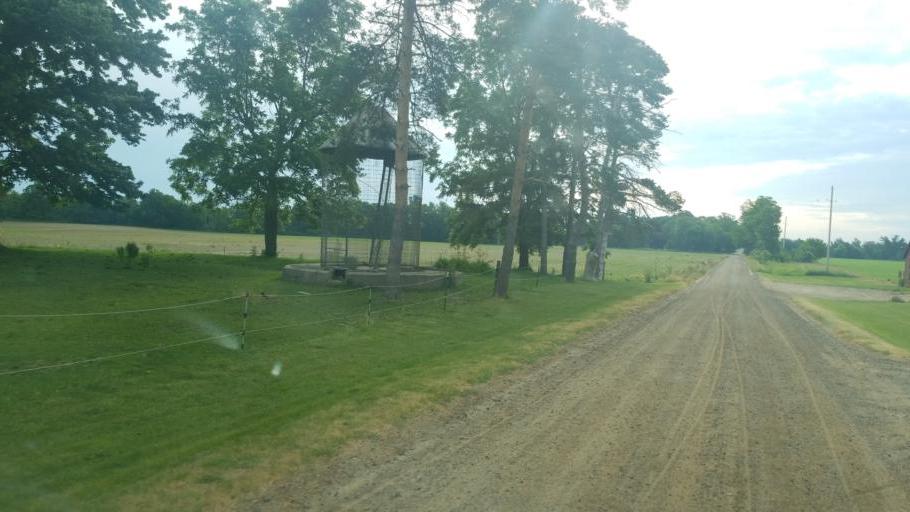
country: US
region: Michigan
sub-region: Eaton County
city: Charlotte
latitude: 42.6118
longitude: -84.9497
